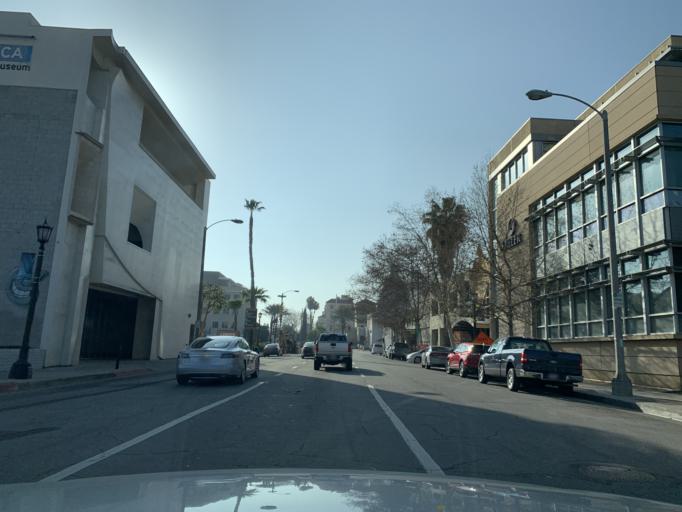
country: US
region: California
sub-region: Los Angeles County
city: Pasadena
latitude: 34.1472
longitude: -118.1399
